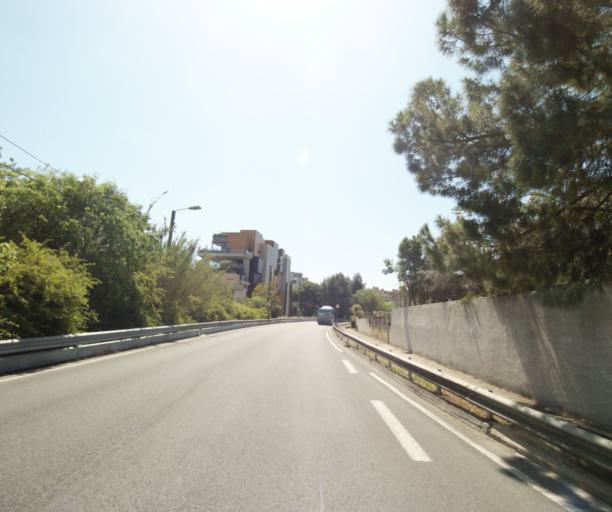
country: FR
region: Languedoc-Roussillon
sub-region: Departement de l'Herault
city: Montpellier
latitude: 43.6012
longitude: 3.8916
